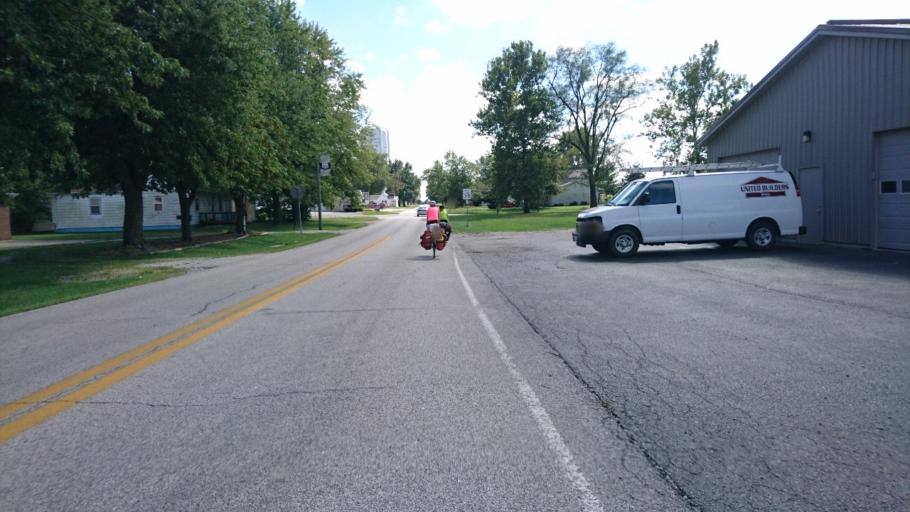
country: US
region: Illinois
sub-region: Montgomery County
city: Litchfield
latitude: 39.1746
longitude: -89.6668
